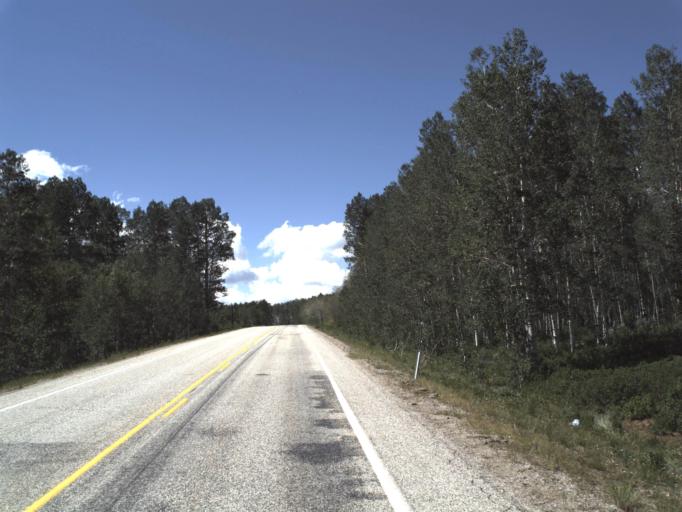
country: US
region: Utah
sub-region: Rich County
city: Randolph
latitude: 41.4718
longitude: -111.4738
